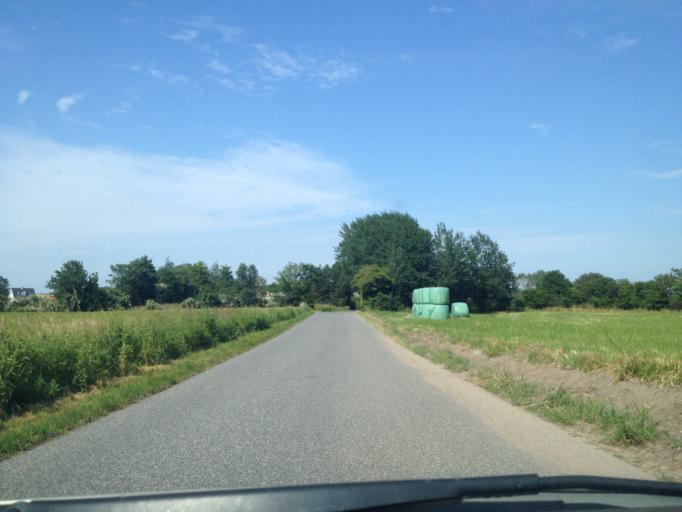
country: DK
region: Central Jutland
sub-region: Samso Kommune
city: Tranebjerg
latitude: 55.8445
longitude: 10.5618
